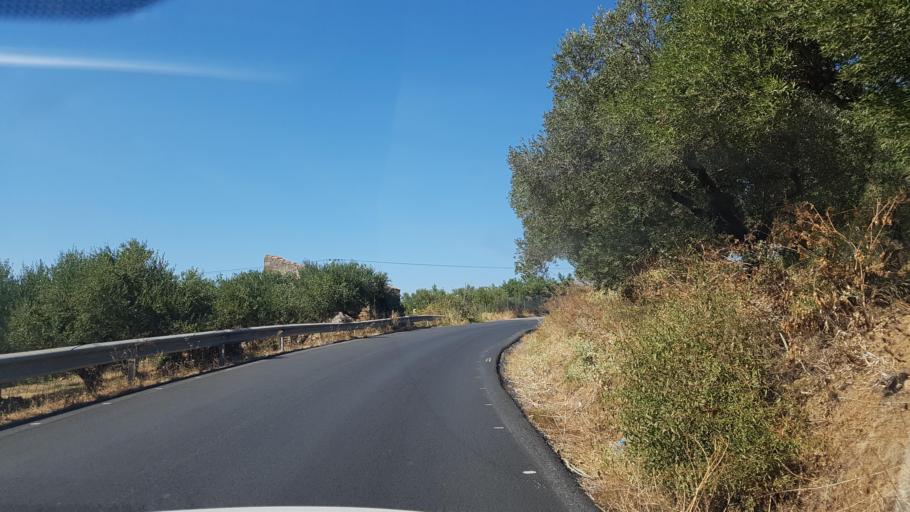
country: GR
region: Crete
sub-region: Nomos Chanias
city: Kissamos
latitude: 35.4898
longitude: 23.6917
